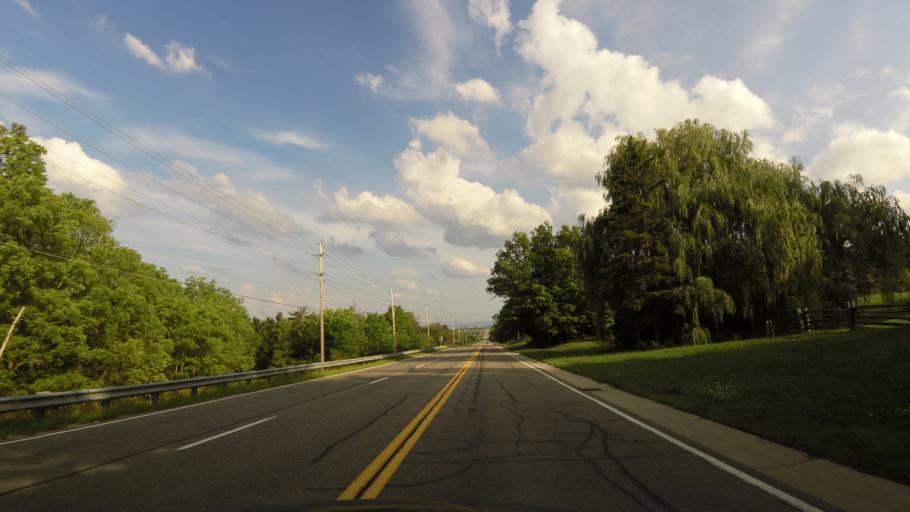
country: CA
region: Ontario
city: Burlington
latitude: 43.3911
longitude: -79.8579
